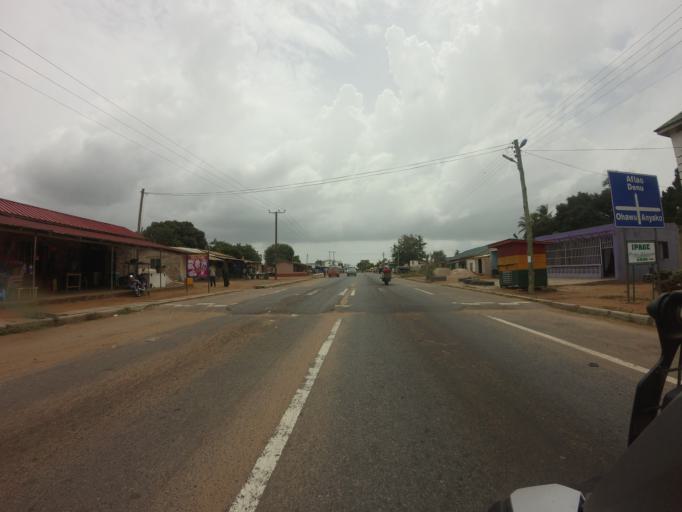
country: GH
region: Volta
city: Keta
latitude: 6.0665
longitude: 0.8604
